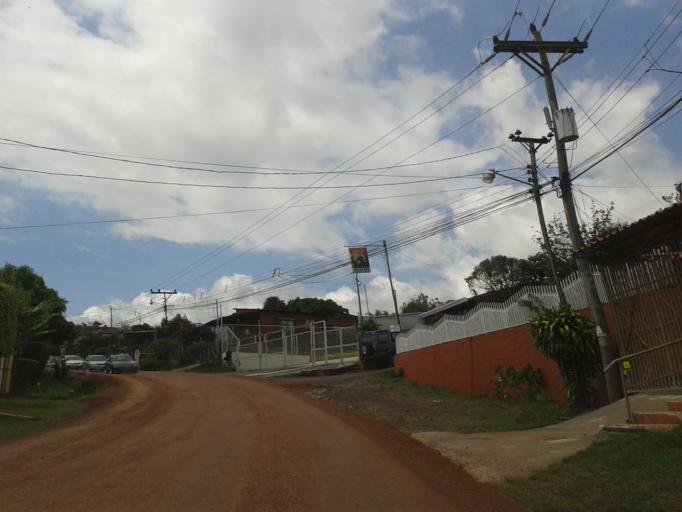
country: CR
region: Alajuela
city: Sabanilla
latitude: 10.0876
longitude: -84.1886
